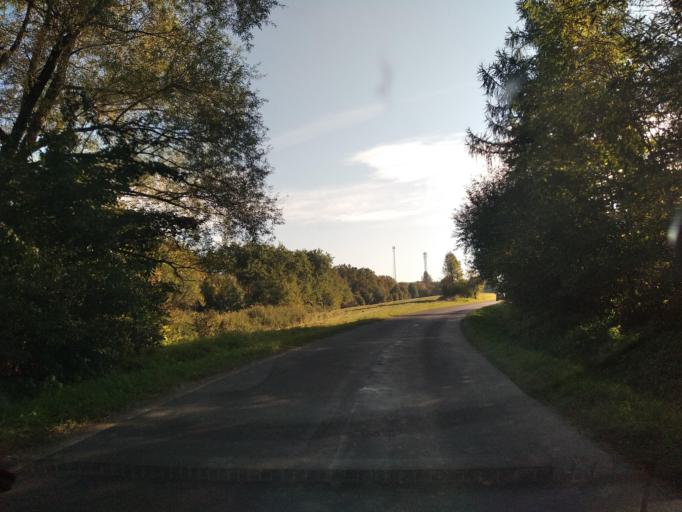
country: PL
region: Subcarpathian Voivodeship
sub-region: Powiat sanocki
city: Besko
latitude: 49.5826
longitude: 21.9521
